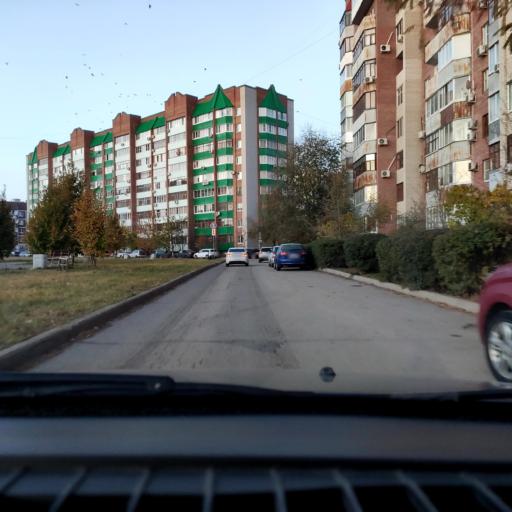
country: RU
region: Samara
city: Tol'yatti
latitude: 53.5449
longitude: 49.3269
